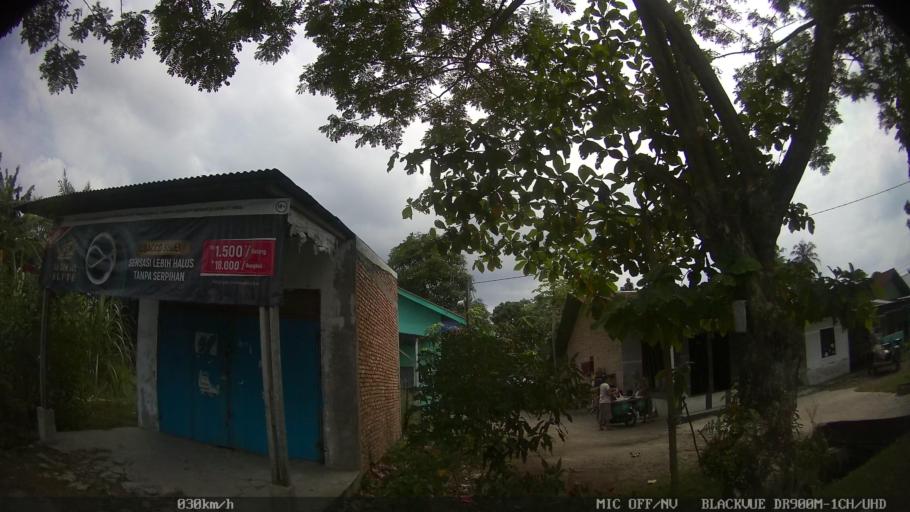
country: ID
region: North Sumatra
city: Sunggal
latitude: 3.6359
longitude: 98.5956
